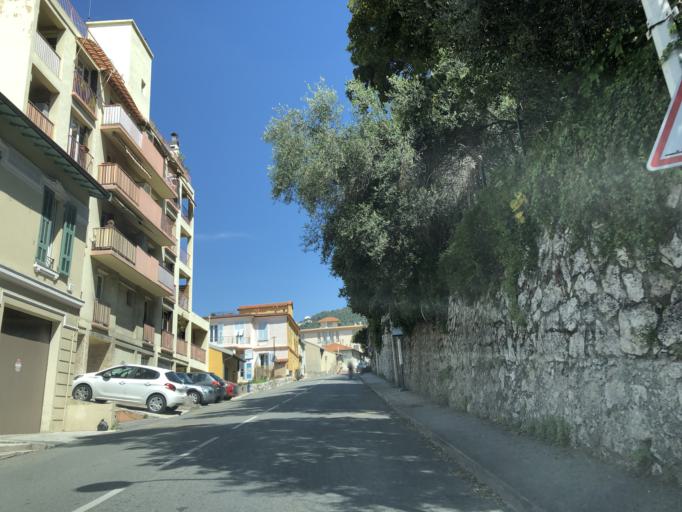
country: FR
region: Provence-Alpes-Cote d'Azur
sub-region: Departement des Alpes-Maritimes
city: Villefranche-sur-Mer
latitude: 43.7094
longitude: 7.2943
